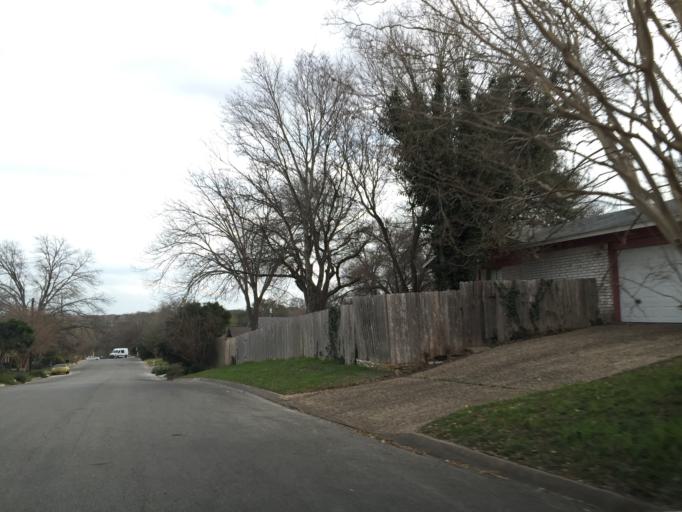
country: US
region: Texas
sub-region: Travis County
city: Wells Branch
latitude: 30.3902
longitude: -97.6807
